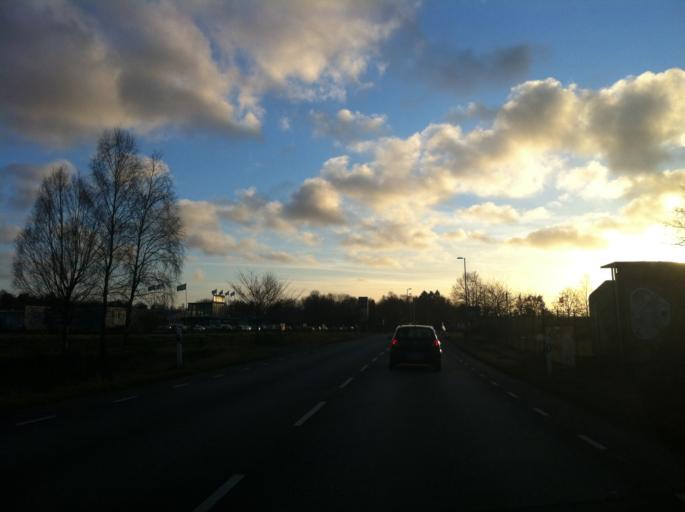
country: SE
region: Skane
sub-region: Hoors Kommun
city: Hoeoer
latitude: 55.9742
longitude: 13.5911
